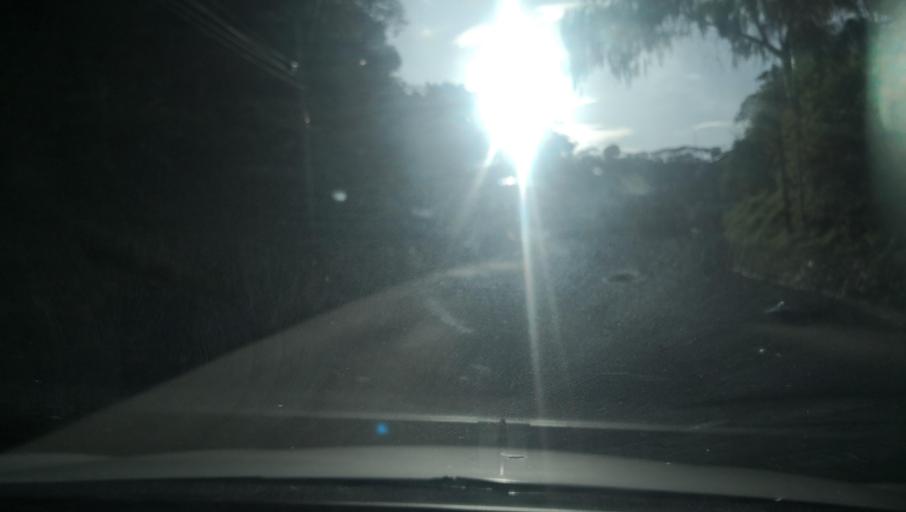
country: HN
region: El Paraiso
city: El Paraiso
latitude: 13.7910
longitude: -86.5688
